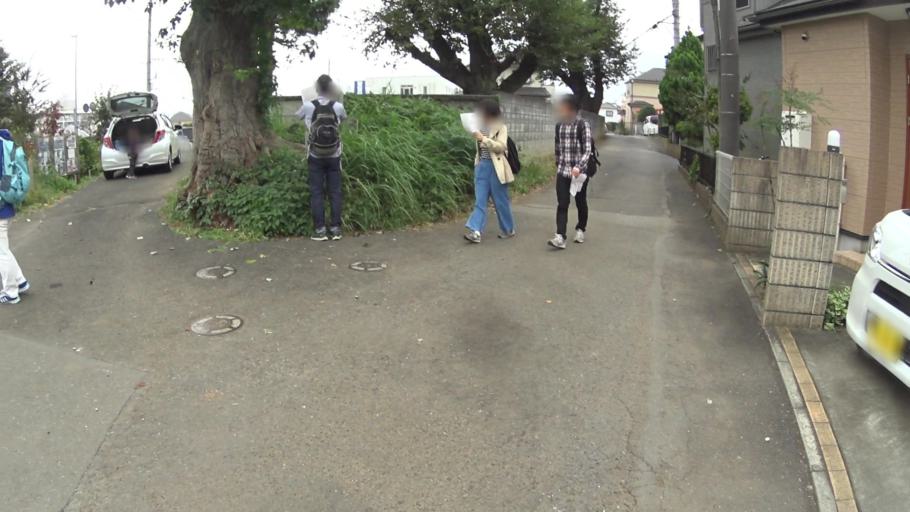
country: JP
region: Saitama
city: Hanno
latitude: 35.8607
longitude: 139.3231
